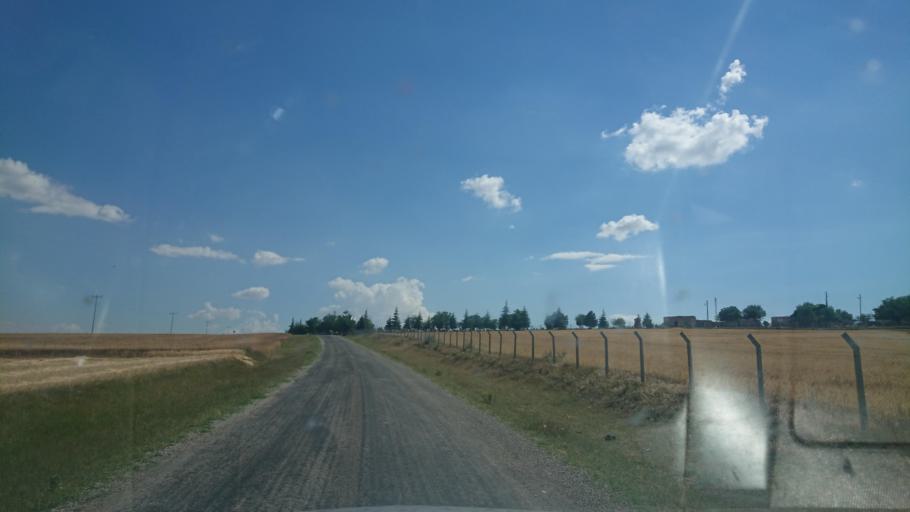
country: TR
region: Aksaray
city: Agacoren
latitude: 38.7649
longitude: 33.7832
